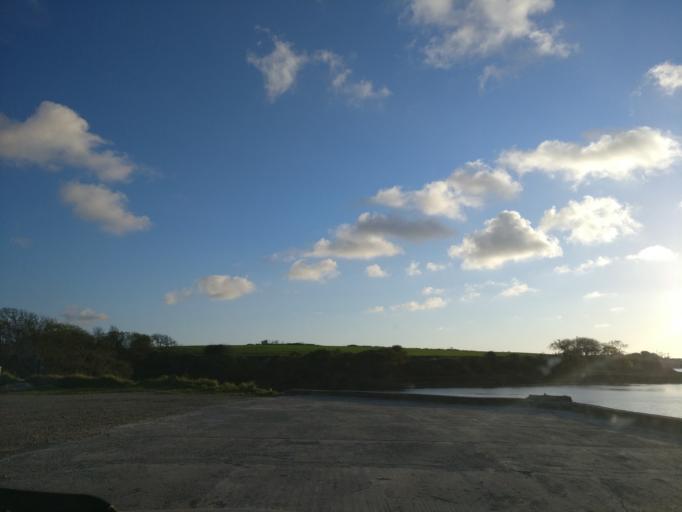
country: FR
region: Brittany
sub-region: Departement du Finistere
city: Lampaul-Plouarzel
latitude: 48.4715
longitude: -4.7464
